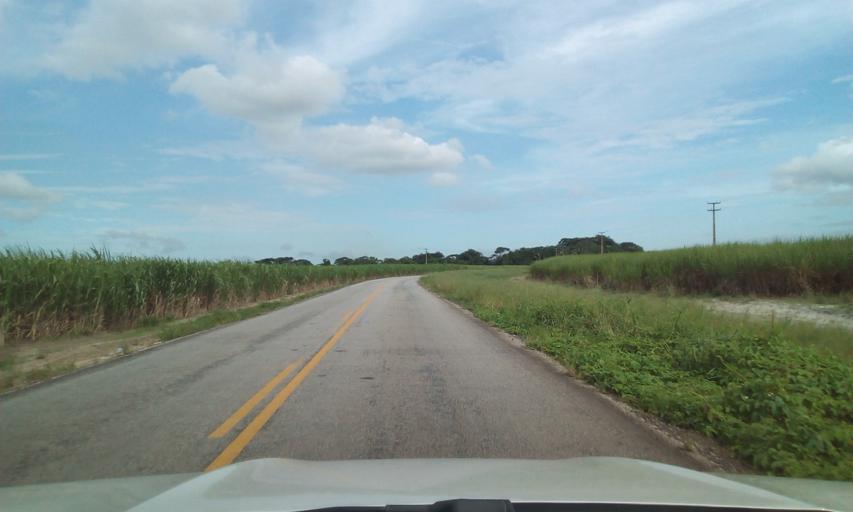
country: BR
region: Paraiba
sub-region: Santa Rita
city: Santa Rita
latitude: -7.0413
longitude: -34.9867
